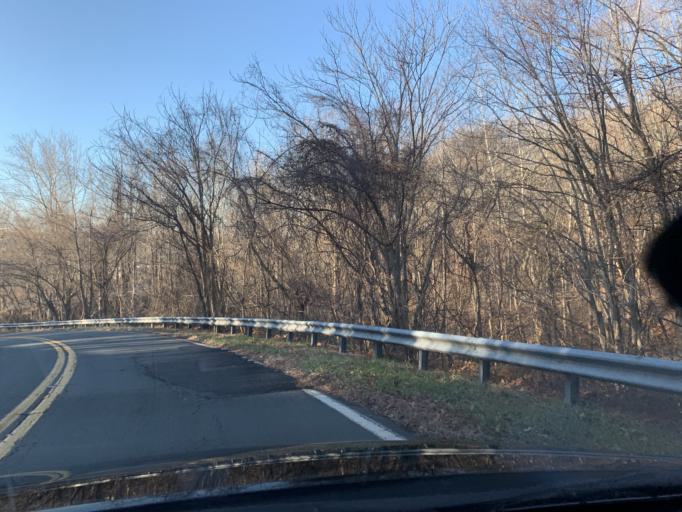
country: US
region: Maryland
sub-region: Montgomery County
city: Cabin John
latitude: 38.9770
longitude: -77.1823
